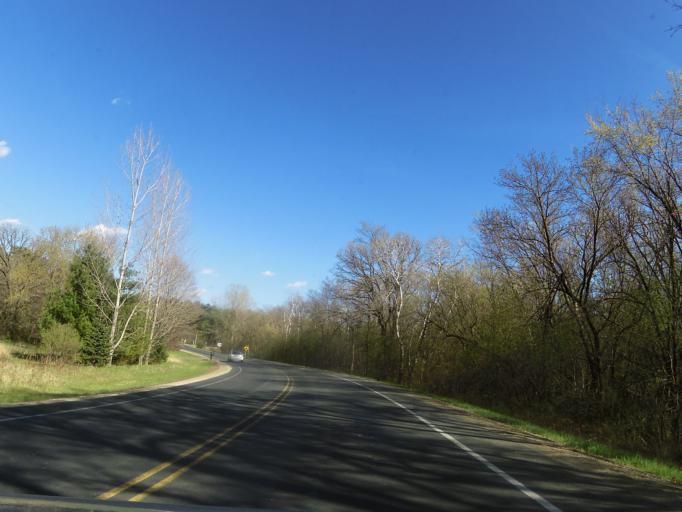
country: US
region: Wisconsin
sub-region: Saint Croix County
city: Somerset
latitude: 45.0263
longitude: -92.6589
